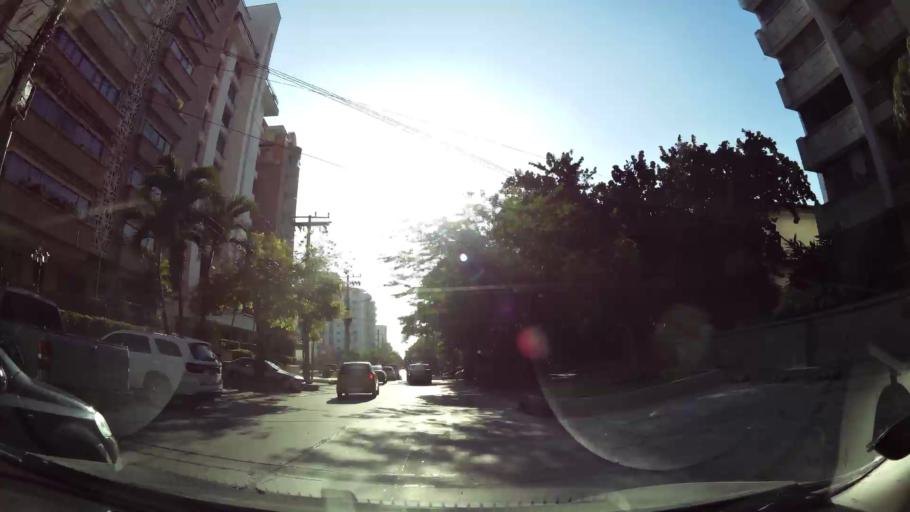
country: CO
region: Atlantico
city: Barranquilla
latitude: 11.0057
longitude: -74.8149
